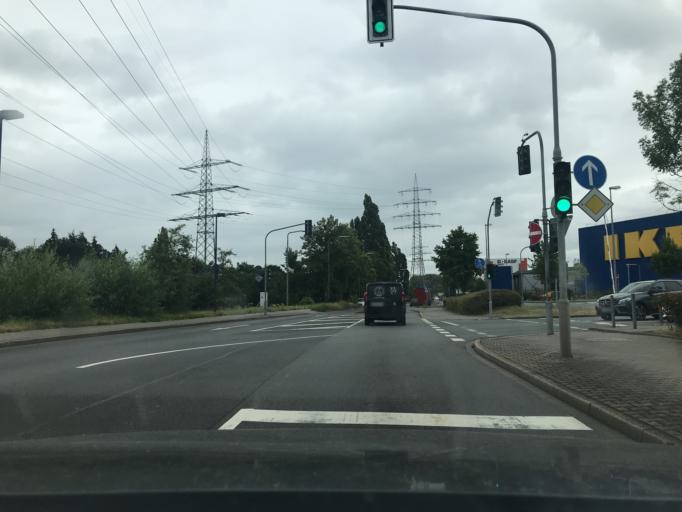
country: DE
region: North Rhine-Westphalia
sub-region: Regierungsbezirk Dusseldorf
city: Erkrath
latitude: 51.1884
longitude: 6.8509
